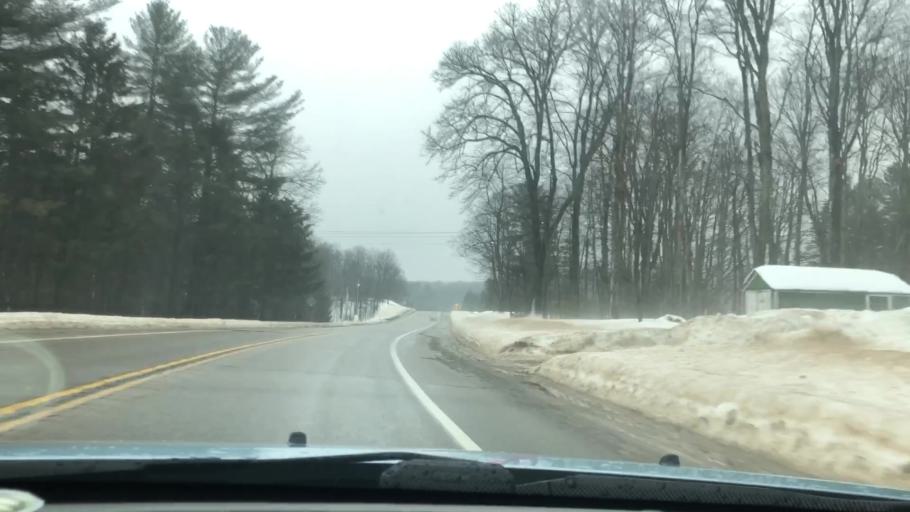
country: US
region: Michigan
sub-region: Otsego County
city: Gaylord
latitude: 45.0613
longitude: -84.7844
